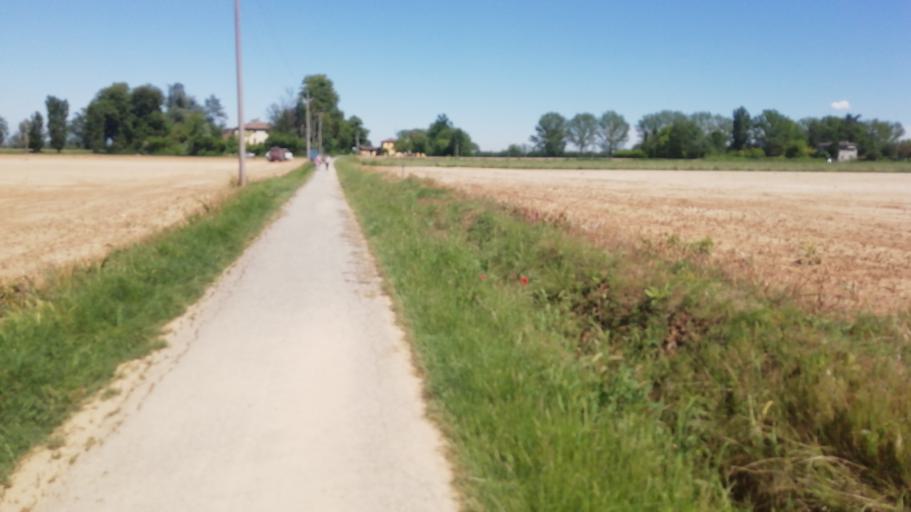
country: IT
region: Emilia-Romagna
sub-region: Provincia di Piacenza
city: Borgonovo Valtidone
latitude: 45.0015
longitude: 9.4541
